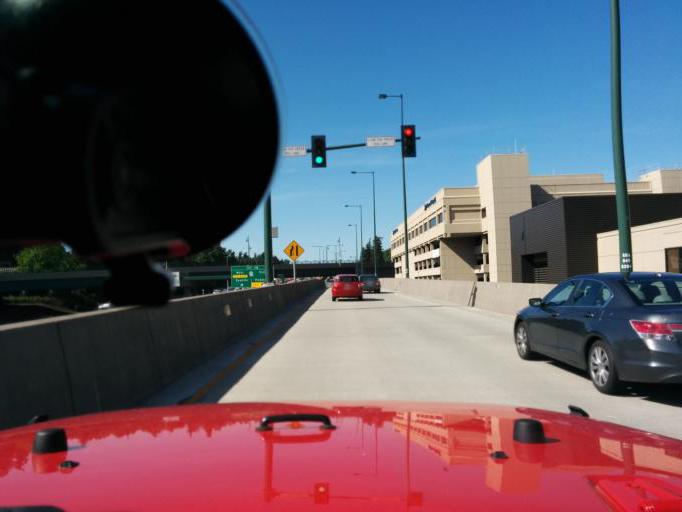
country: US
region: Washington
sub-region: King County
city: Bellevue
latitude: 47.6203
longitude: -122.1883
